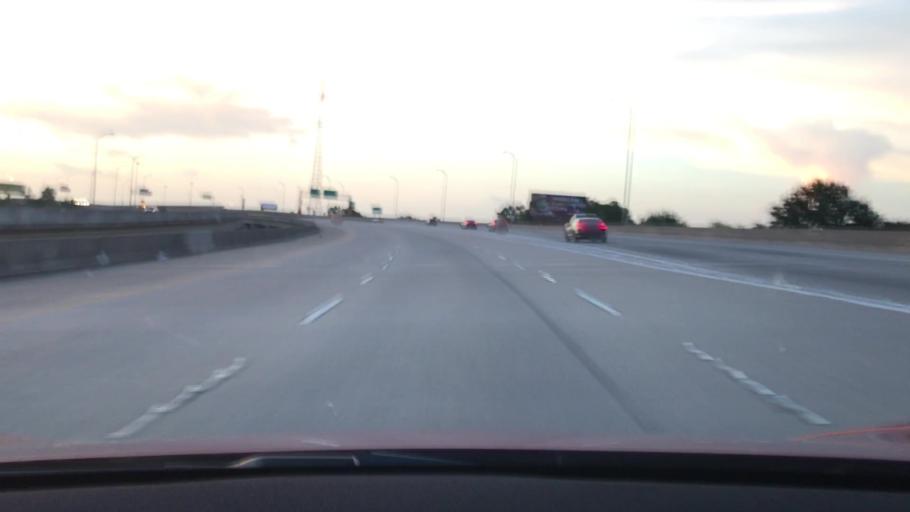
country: US
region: Louisiana
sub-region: Bossier Parish
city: Bossier City
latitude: 32.4901
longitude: -93.7551
